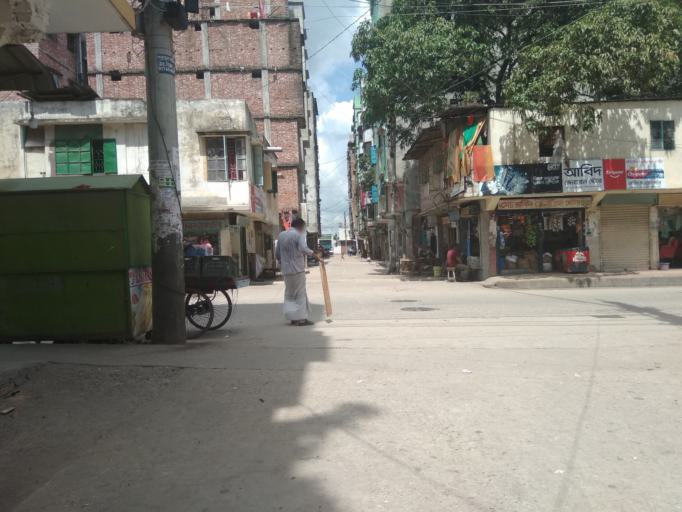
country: BD
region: Dhaka
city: Tungi
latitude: 23.8166
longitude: 90.3630
